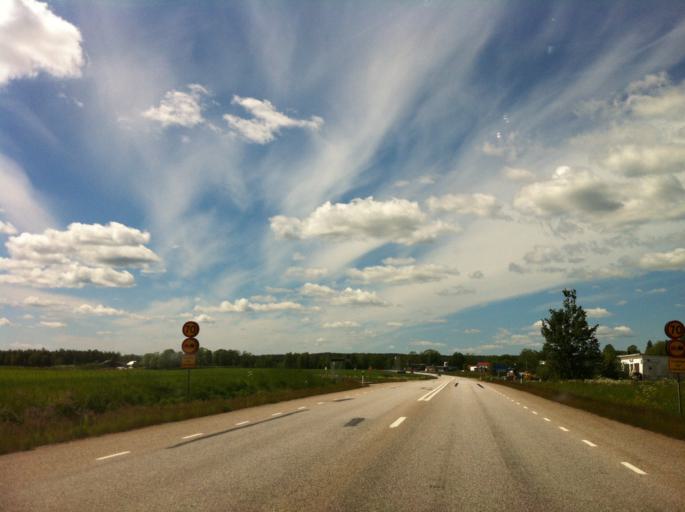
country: SE
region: Vaestra Goetaland
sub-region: Amals Kommun
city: Amal
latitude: 58.9790
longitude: 12.6383
